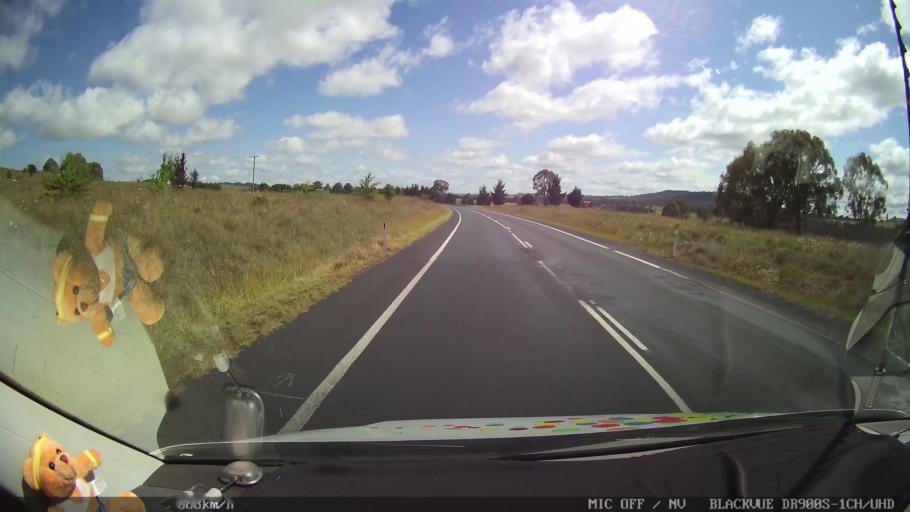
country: AU
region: New South Wales
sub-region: Glen Innes Severn
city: Glen Innes
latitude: -29.8867
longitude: 151.7336
